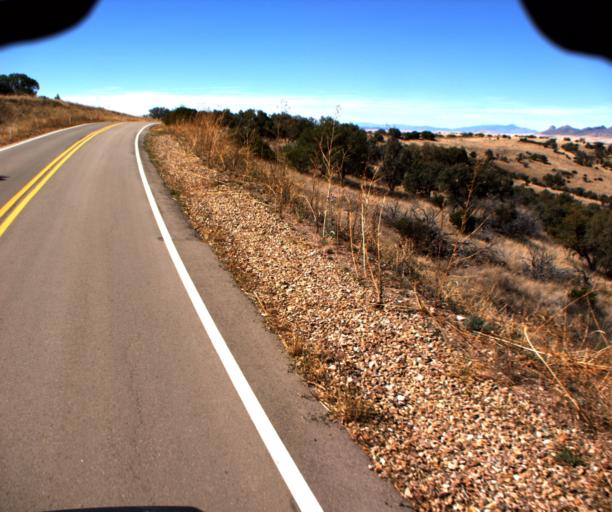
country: US
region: Arizona
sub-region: Cochise County
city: Huachuca City
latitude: 31.5244
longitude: -110.5016
